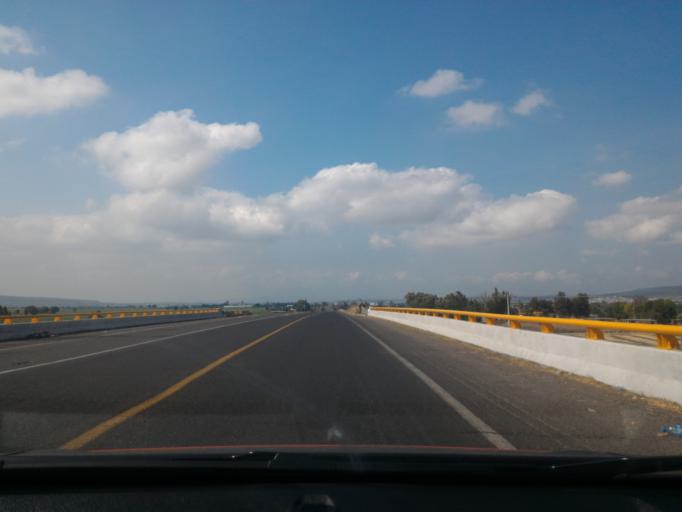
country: MX
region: Guanajuato
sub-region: Penjamo
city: Estacion la Piedad
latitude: 20.3976
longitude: -101.9995
